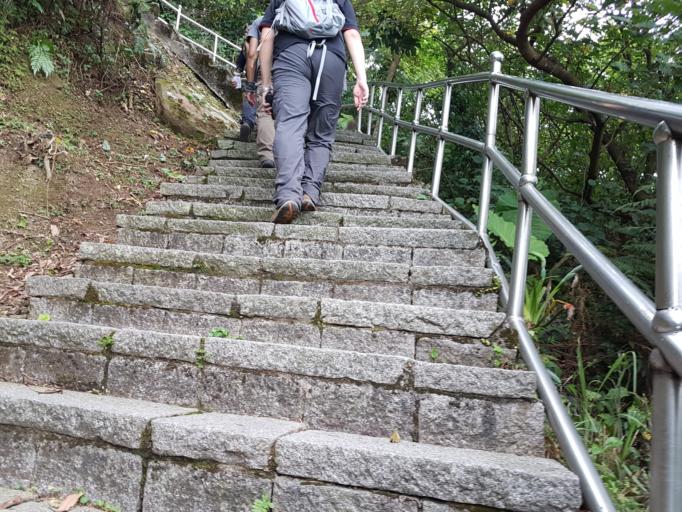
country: TW
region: Taiwan
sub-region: Keelung
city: Keelung
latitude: 25.0538
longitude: 121.6632
